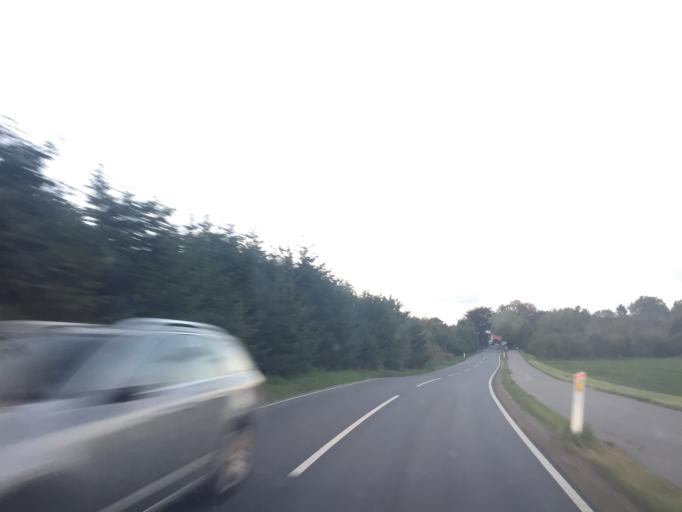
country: DK
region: Capital Region
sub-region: Hoje-Taastrup Kommune
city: Flong
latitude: 55.6750
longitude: 12.1873
